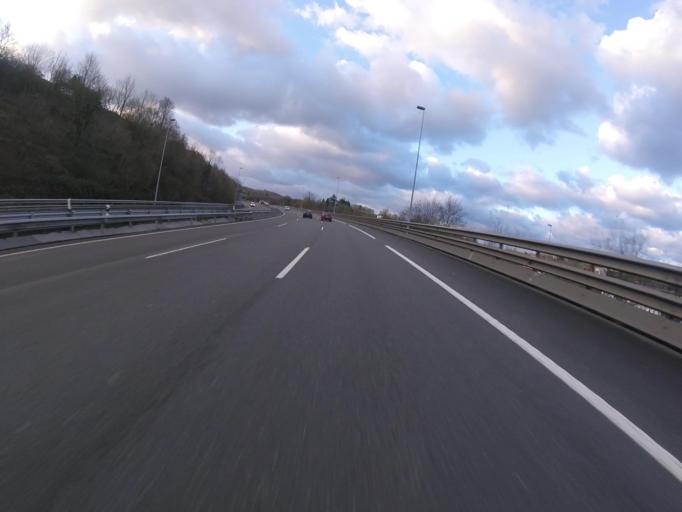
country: ES
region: Basque Country
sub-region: Provincia de Guipuzcoa
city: Errenteria
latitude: 43.3134
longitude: -1.9171
